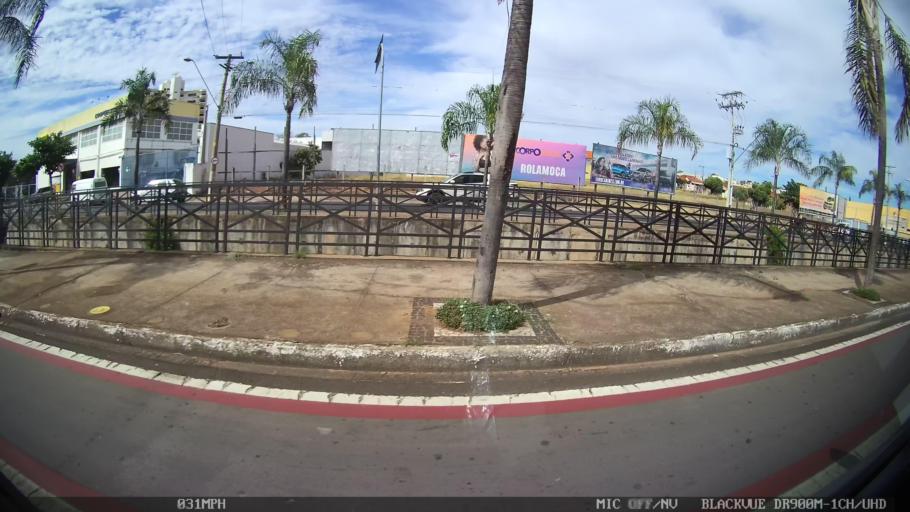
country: BR
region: Sao Paulo
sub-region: Catanduva
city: Catanduva
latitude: -21.1418
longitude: -48.9697
